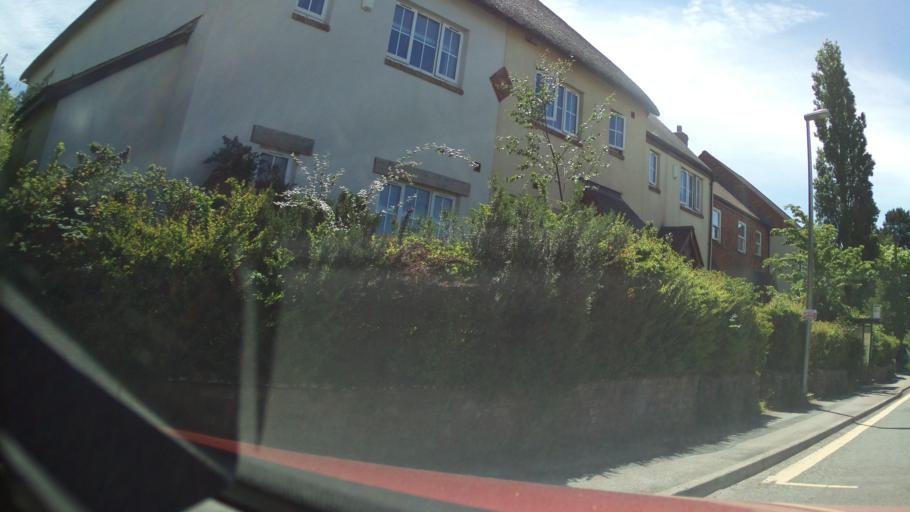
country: GB
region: England
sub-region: Devon
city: Ottery St Mary
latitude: 50.7727
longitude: -3.2580
